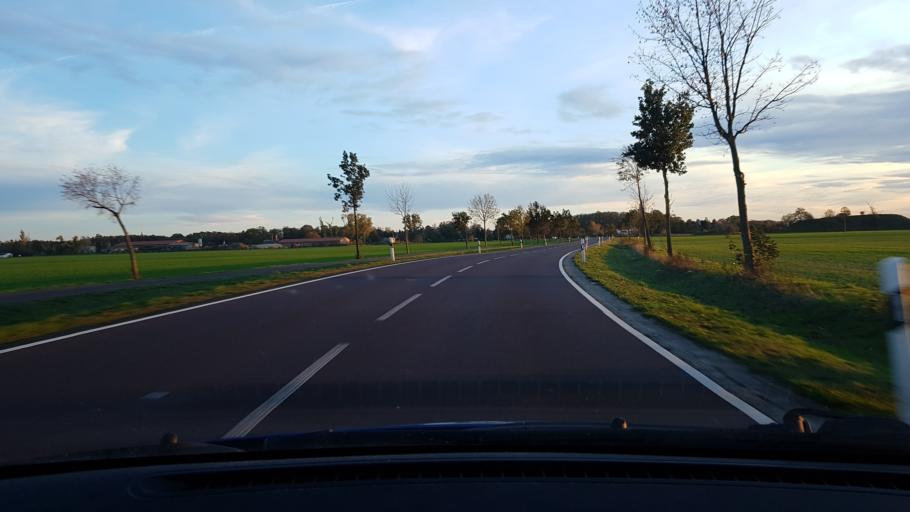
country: DE
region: Saxony-Anhalt
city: Wahlitz
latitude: 52.1261
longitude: 11.7628
